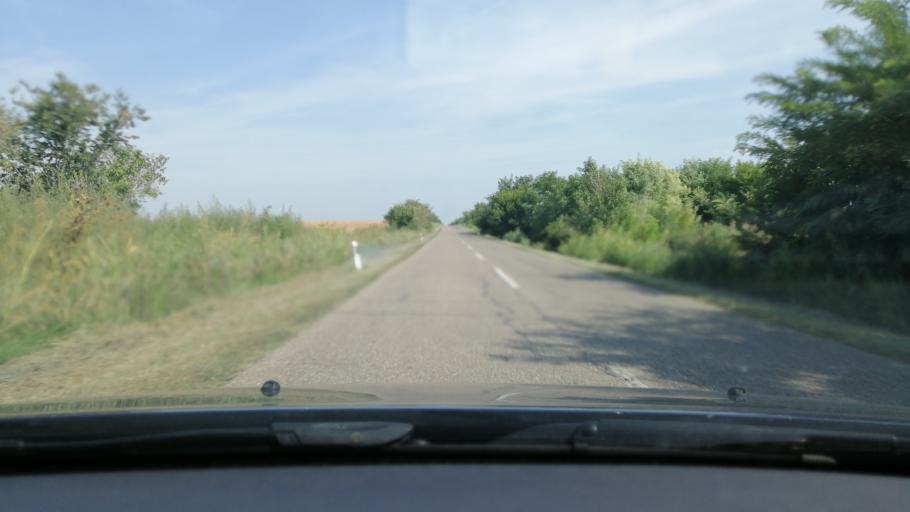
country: RS
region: Autonomna Pokrajina Vojvodina
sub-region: Juznobanatski Okrug
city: Kovacica
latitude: 45.1334
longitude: 20.6161
